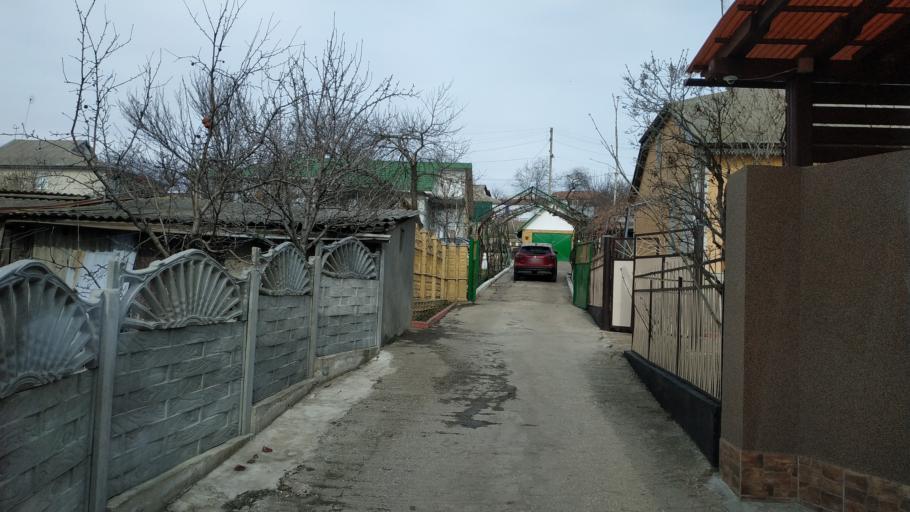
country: MD
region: Chisinau
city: Vatra
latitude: 47.0944
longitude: 28.6719
